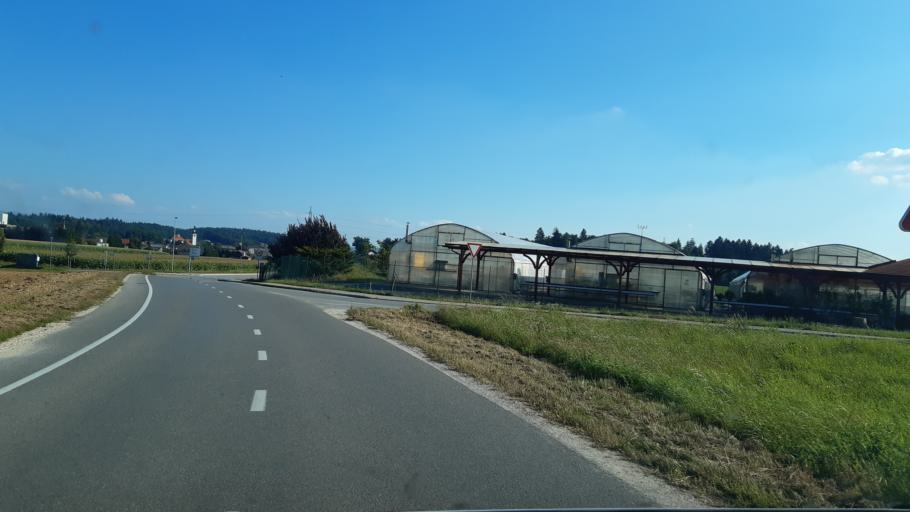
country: SI
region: Ivancna Gorica
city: Ivancna Gorica
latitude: 45.9464
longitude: 14.8028
